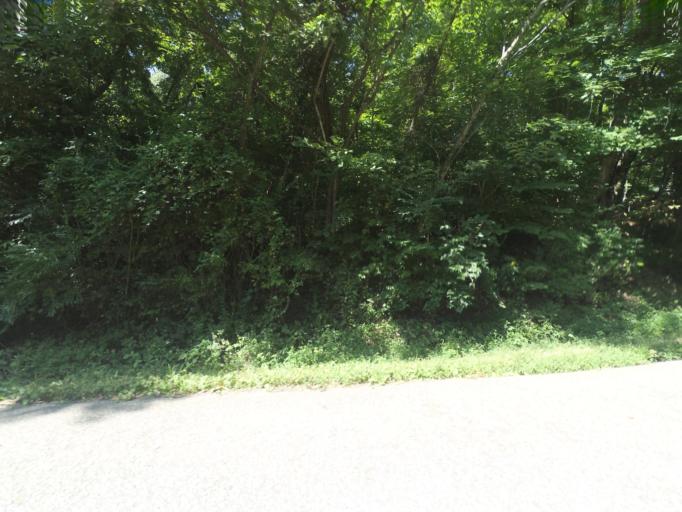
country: US
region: West Virginia
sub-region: Cabell County
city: Huntington
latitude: 38.4361
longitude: -82.4332
